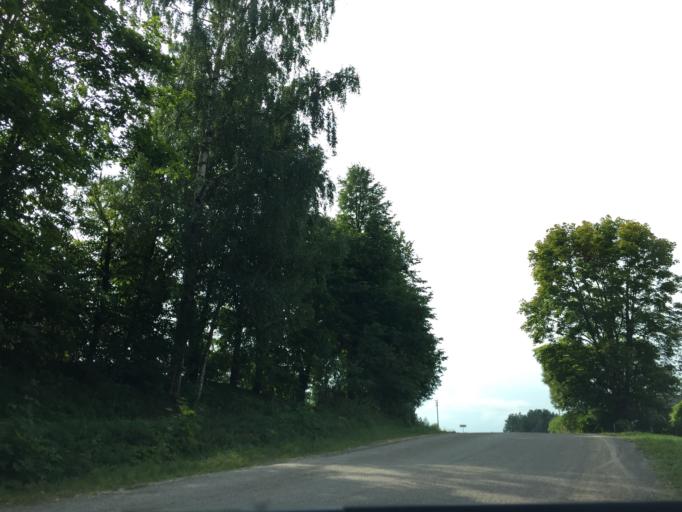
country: LV
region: Cibla
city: Cibla
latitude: 56.2764
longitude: 27.8211
